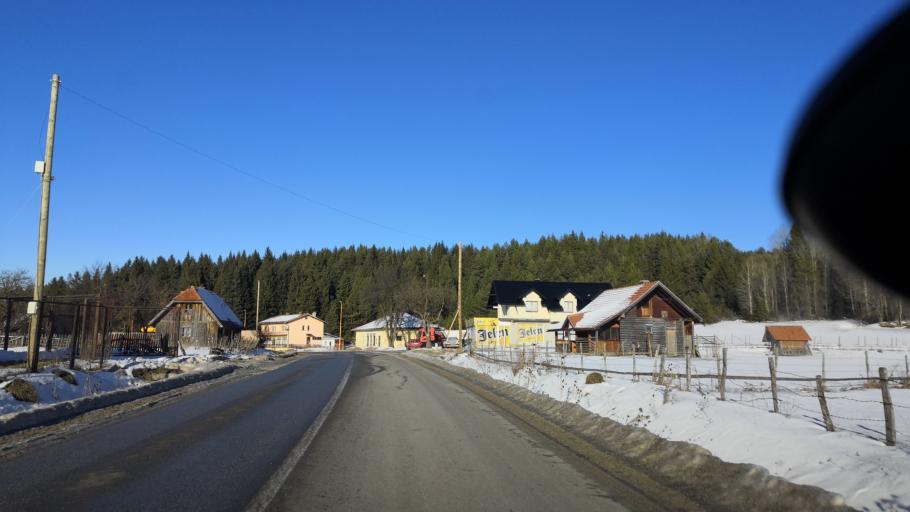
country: BA
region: Republika Srpska
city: Sokolac
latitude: 43.9965
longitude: 18.8827
